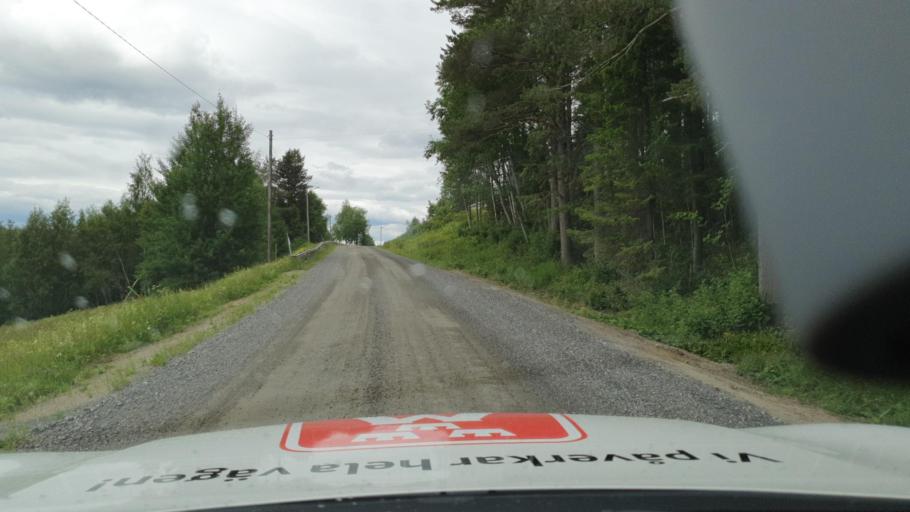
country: SE
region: Vaesterbotten
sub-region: Nordmalings Kommun
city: Nordmaling
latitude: 63.6739
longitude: 19.4379
